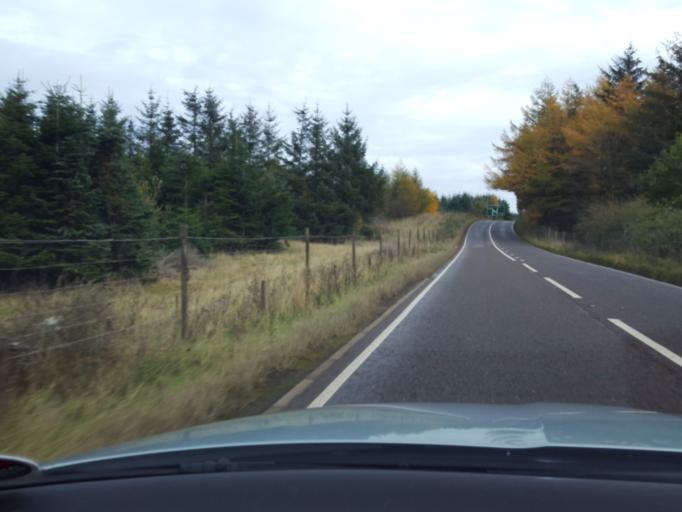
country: GB
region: Scotland
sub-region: South Lanarkshire
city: Biggar
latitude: 55.6830
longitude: -3.4610
